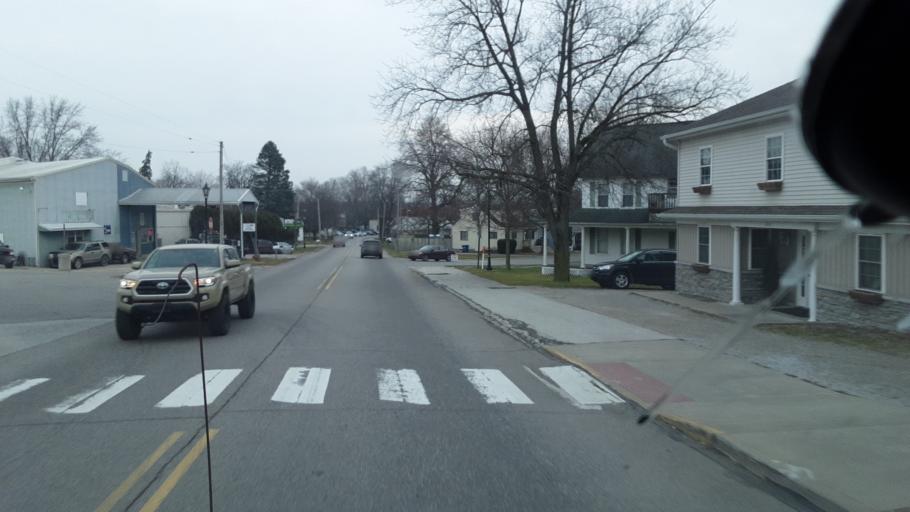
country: US
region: Indiana
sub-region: Elkhart County
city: Middlebury
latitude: 41.6738
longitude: -85.7090
